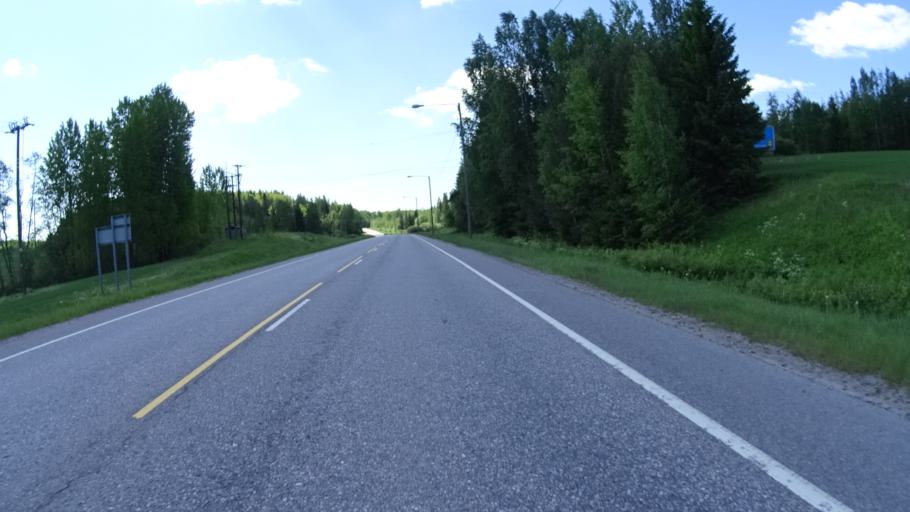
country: FI
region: Uusimaa
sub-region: Helsinki
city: Nurmijaervi
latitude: 60.3934
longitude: 24.8113
